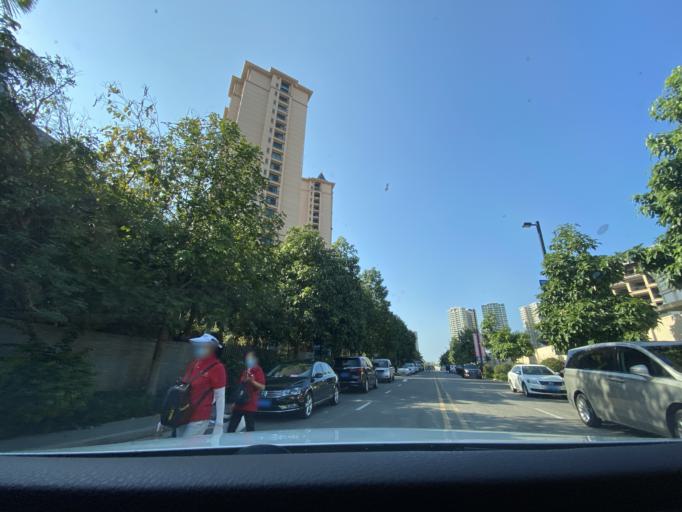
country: CN
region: Hainan
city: Yingzhou
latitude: 18.4077
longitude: 109.8815
